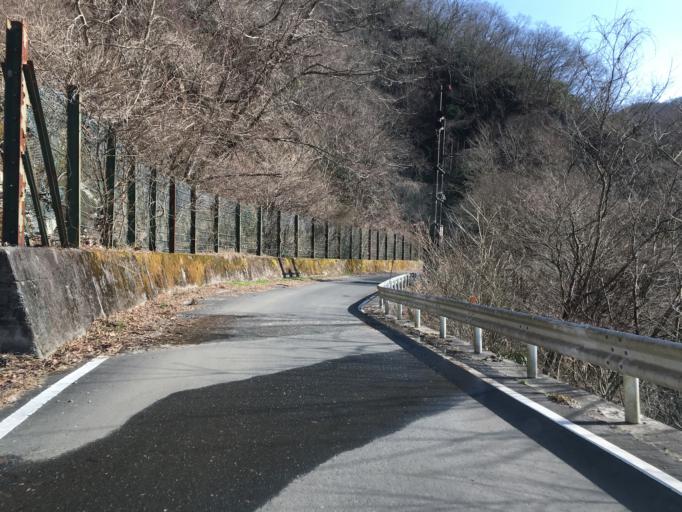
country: JP
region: Ibaraki
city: Kitaibaraki
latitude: 36.7886
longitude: 140.6634
